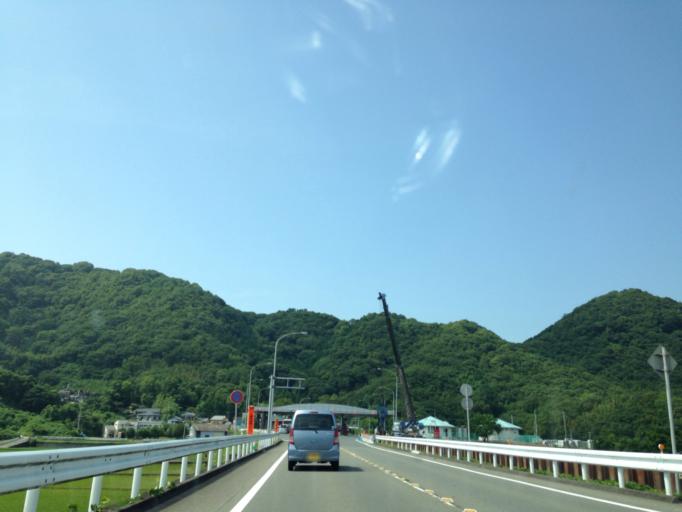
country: JP
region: Shizuoka
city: Mishima
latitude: 35.0565
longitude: 138.9236
